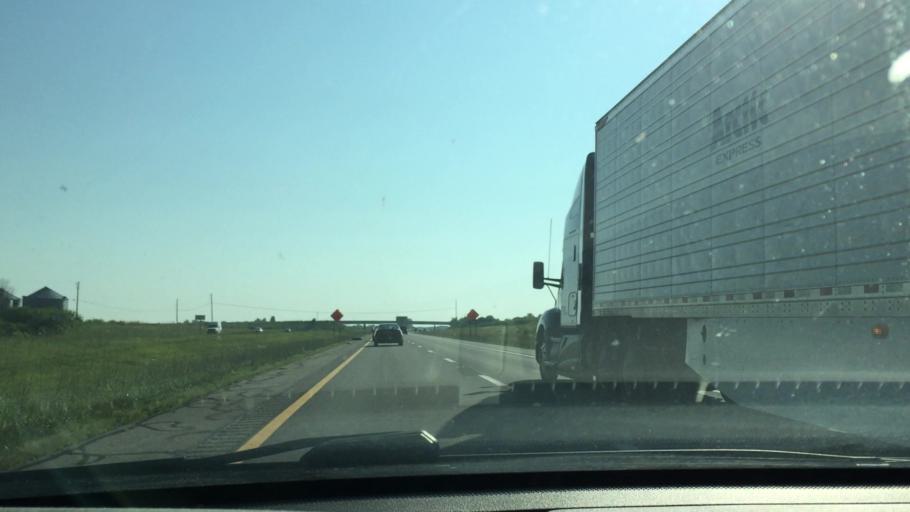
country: US
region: Ohio
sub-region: Madison County
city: Bethel
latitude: 39.7324
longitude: -83.3656
